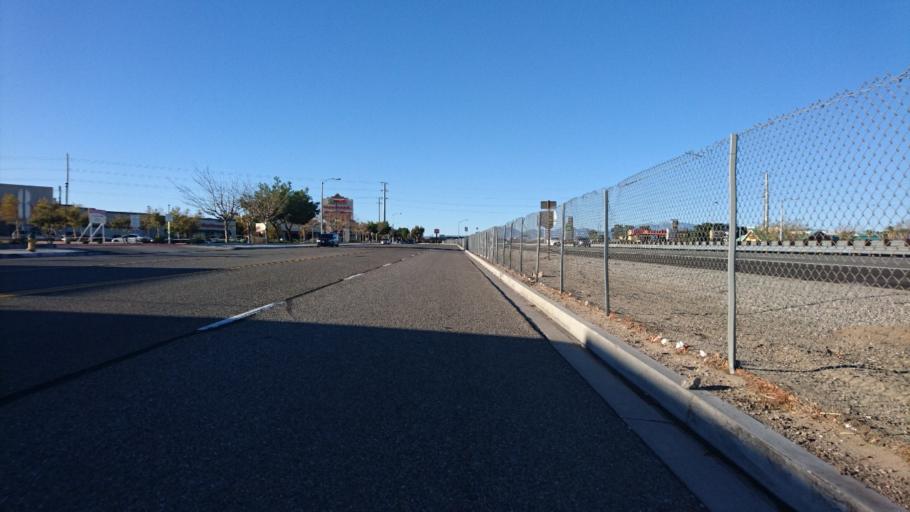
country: US
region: California
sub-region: San Bernardino County
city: Mountain View Acres
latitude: 34.4763
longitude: -117.3413
